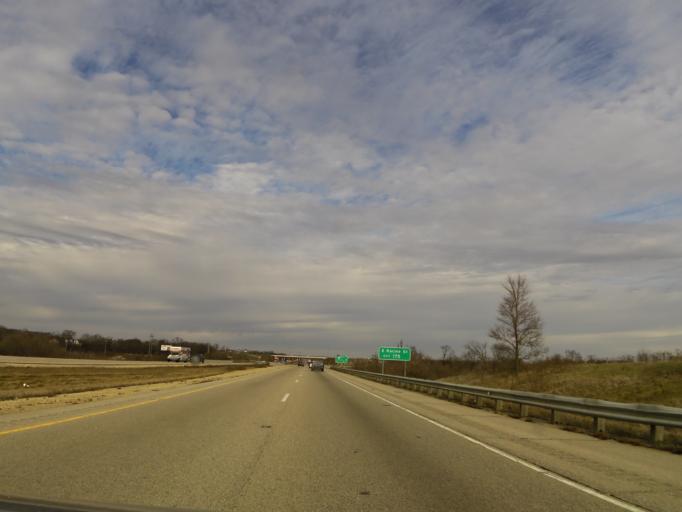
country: US
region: Wisconsin
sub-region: Rock County
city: Janesville
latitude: 42.6639
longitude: -88.9833
